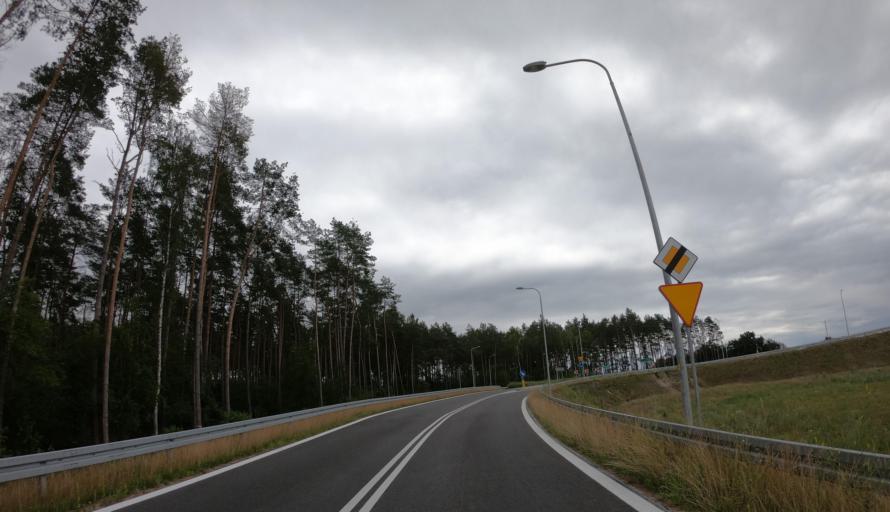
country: PL
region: West Pomeranian Voivodeship
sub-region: Powiat goleniowski
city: Goleniow
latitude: 53.6257
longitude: 14.8203
